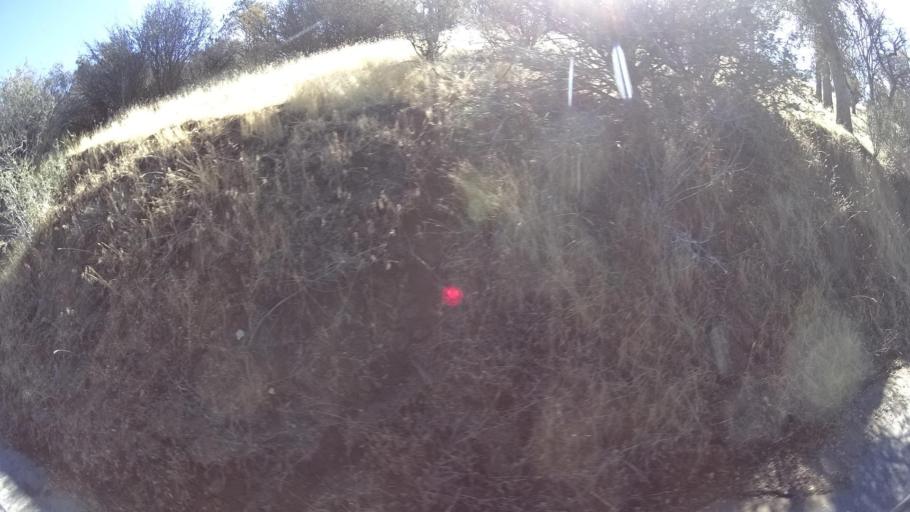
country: US
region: California
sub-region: Kern County
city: Bodfish
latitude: 35.4393
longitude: -118.6968
